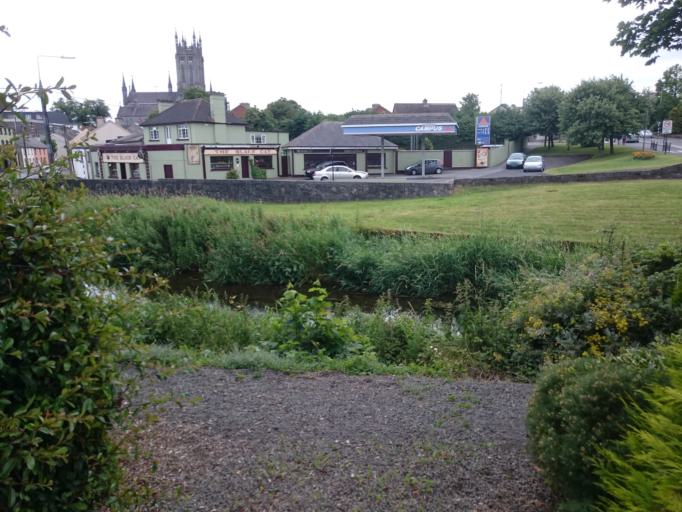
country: IE
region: Leinster
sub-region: Kilkenny
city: Kilkenny
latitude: 52.6544
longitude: -7.2599
